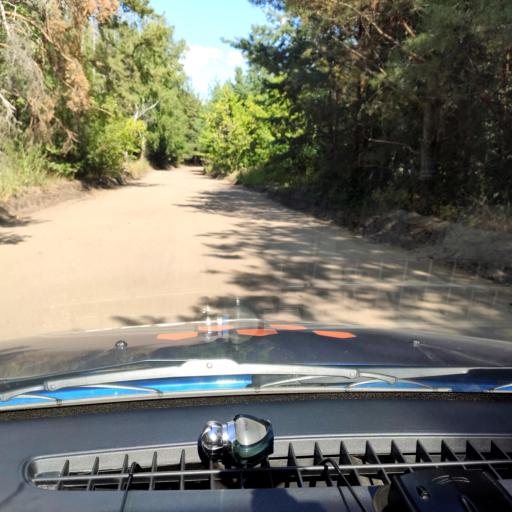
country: RU
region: Voronezj
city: Somovo
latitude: 51.7200
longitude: 39.3894
